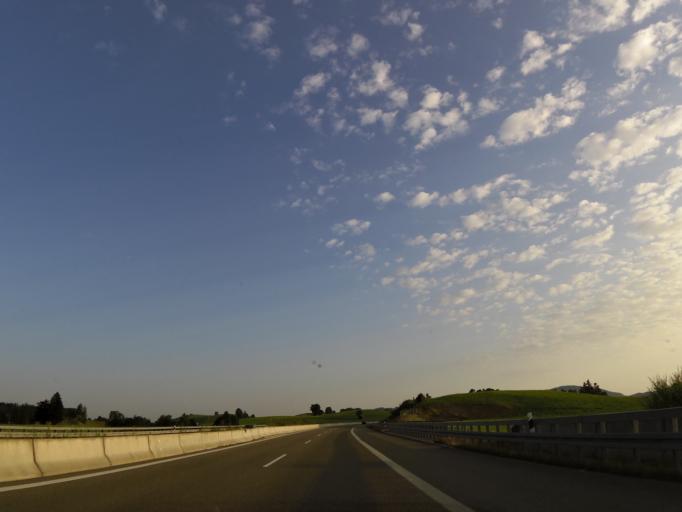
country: DE
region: Bavaria
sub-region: Swabia
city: Hopferau
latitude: 47.5886
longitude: 10.6585
